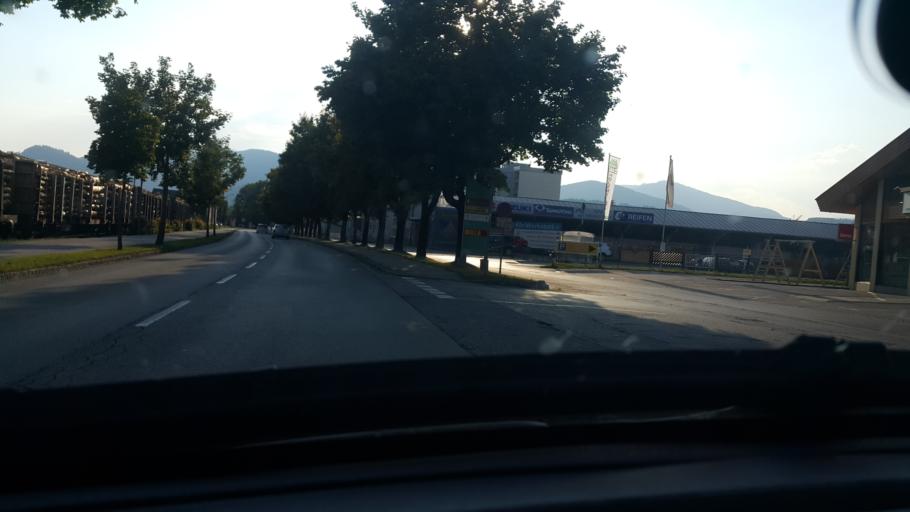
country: AT
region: Carinthia
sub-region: Politischer Bezirk Feldkirchen
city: Feldkirchen in Karnten
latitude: 46.7222
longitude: 14.1022
